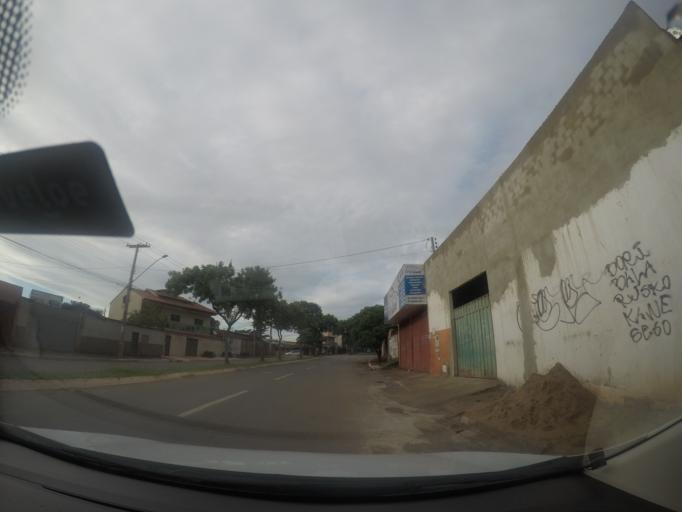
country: BR
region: Goias
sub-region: Goiania
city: Goiania
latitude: -16.6118
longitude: -49.3421
